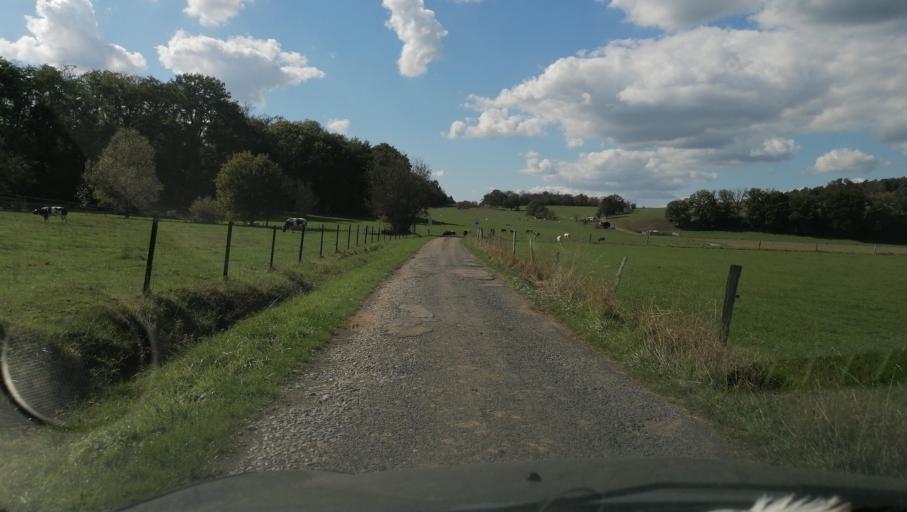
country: BE
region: Wallonia
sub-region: Province de Namur
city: Rochefort
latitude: 50.1247
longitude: 5.1727
